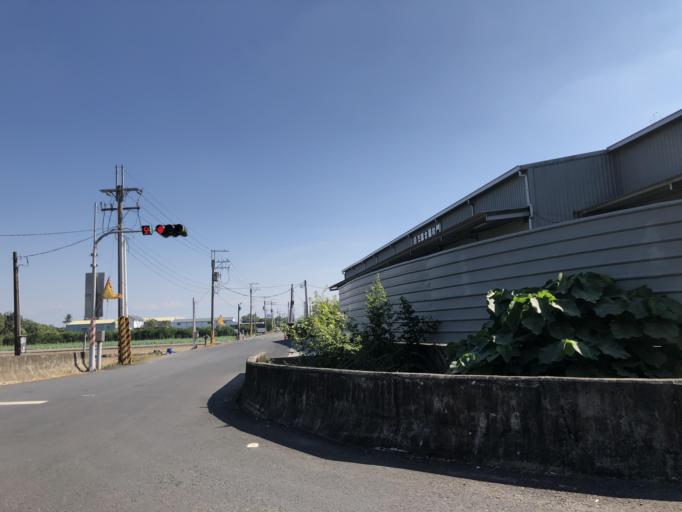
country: TW
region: Taiwan
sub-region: Tainan
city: Tainan
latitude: 23.0127
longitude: 120.2879
